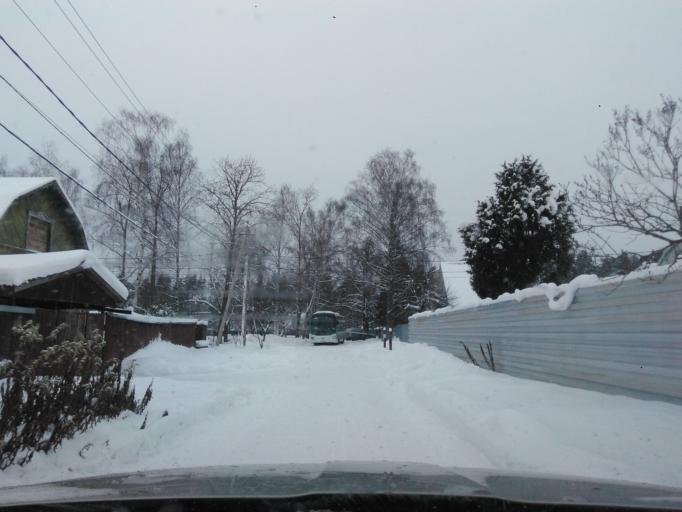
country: RU
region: Moskovskaya
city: Lozhki
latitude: 56.0493
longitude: 37.1042
